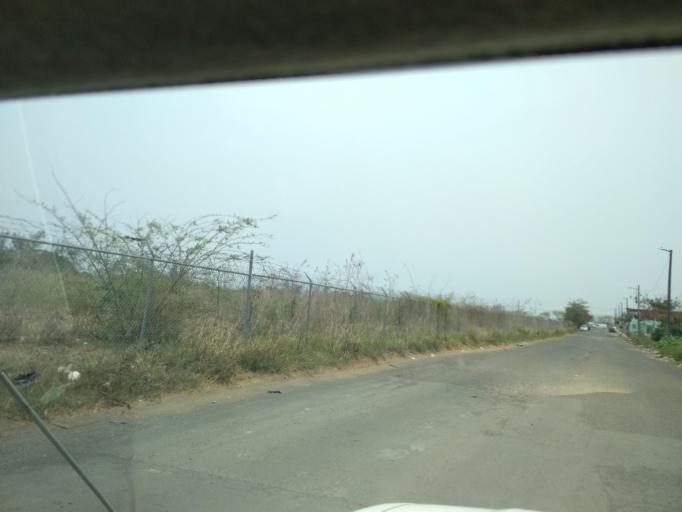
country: MX
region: Veracruz
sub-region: Veracruz
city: Las Amapolas
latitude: 19.1527
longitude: -96.2141
